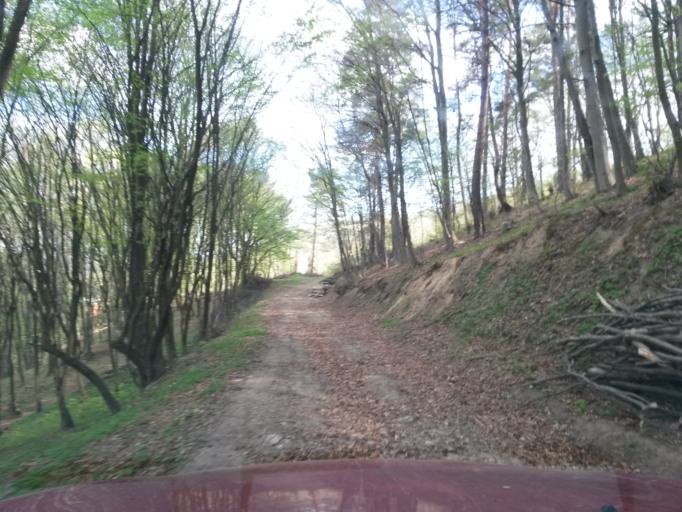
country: SK
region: Presovsky
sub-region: Okres Presov
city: Presov
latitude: 48.9476
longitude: 21.1607
